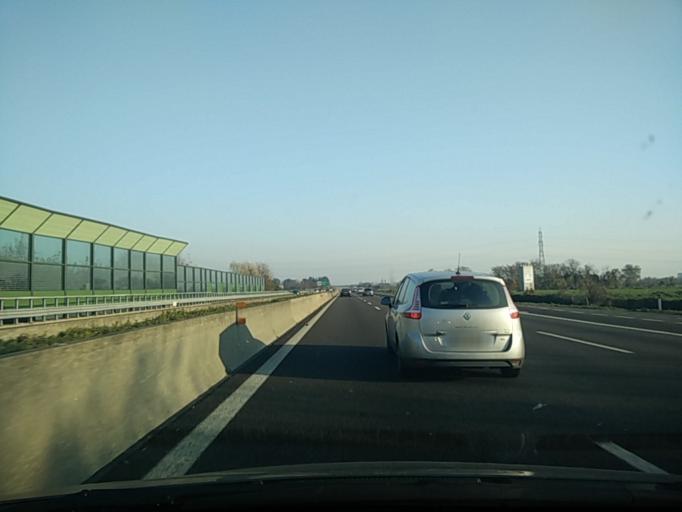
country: IT
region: Lombardy
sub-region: Provincia di Bergamo
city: Costa di Mezzate
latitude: 45.6460
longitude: 9.7961
